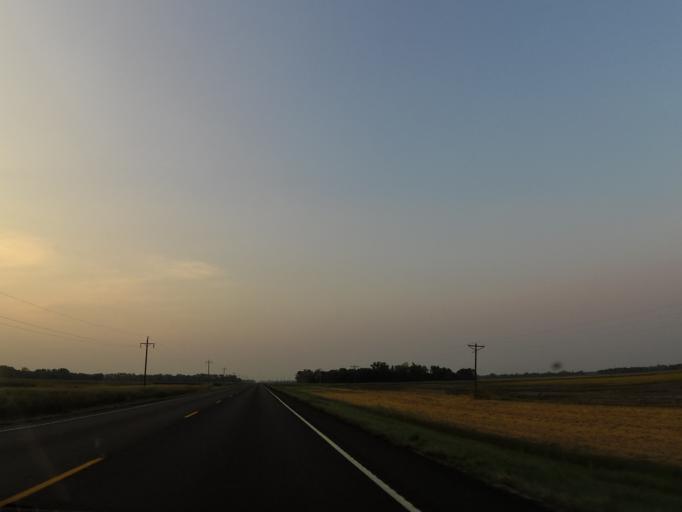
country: US
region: North Dakota
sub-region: Walsh County
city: Park River
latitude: 48.2865
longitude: -97.6224
